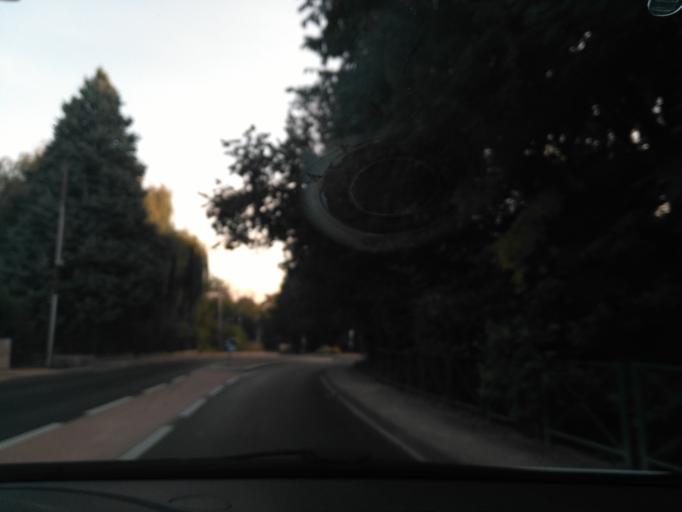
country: FR
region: Rhone-Alpes
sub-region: Departement du Rhone
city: Albigny-sur-Saone
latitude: 45.8712
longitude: 4.8210
